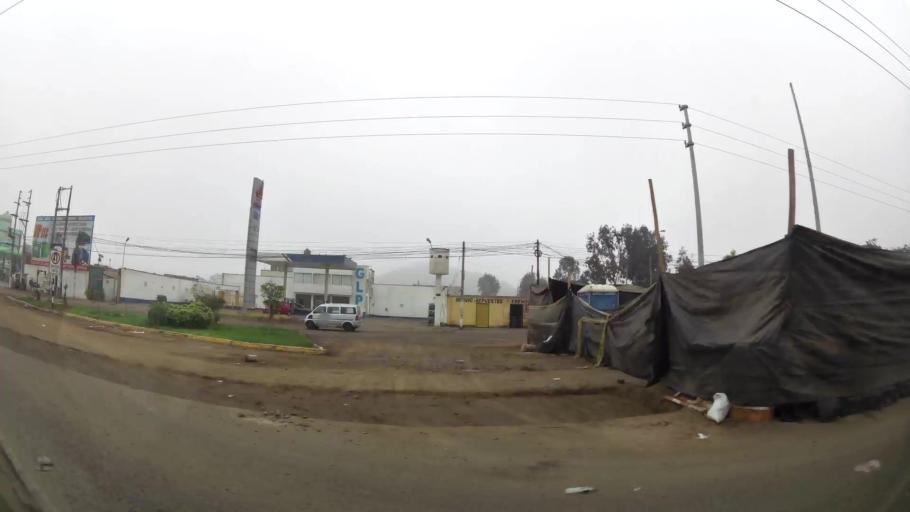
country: PE
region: Lima
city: Ventanilla
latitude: -11.8410
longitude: -77.1043
